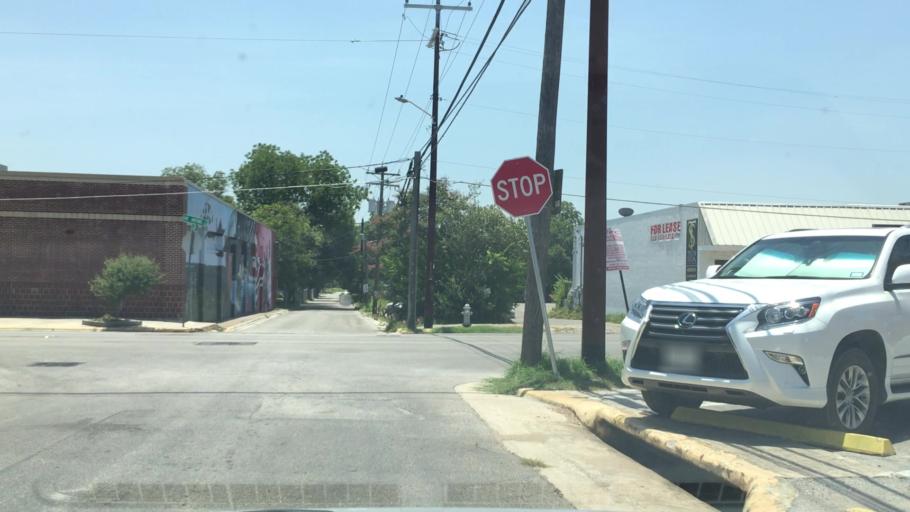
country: US
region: Texas
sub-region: Hays County
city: San Marcos
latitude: 29.8822
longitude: -97.9426
